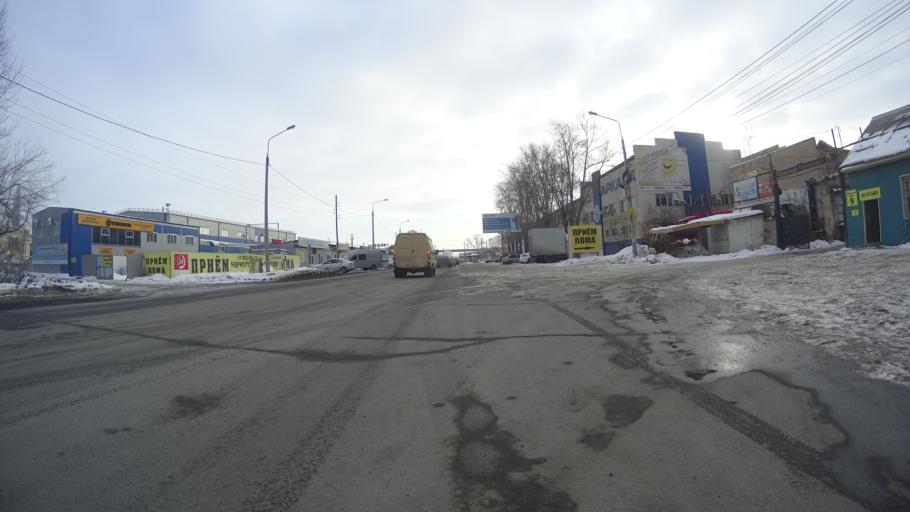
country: RU
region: Chelyabinsk
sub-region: Gorod Chelyabinsk
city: Chelyabinsk
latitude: 55.1222
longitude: 61.3860
